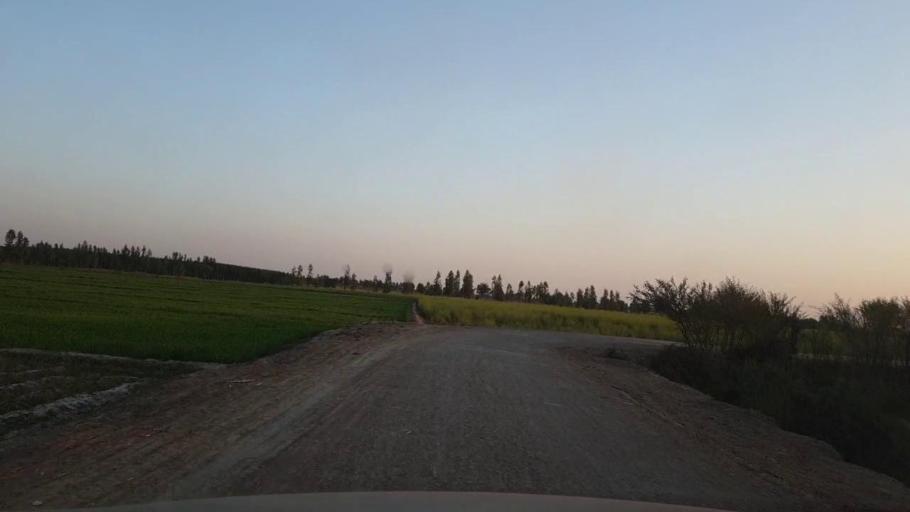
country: PK
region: Sindh
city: Tando Allahyar
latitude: 25.5545
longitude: 68.6418
